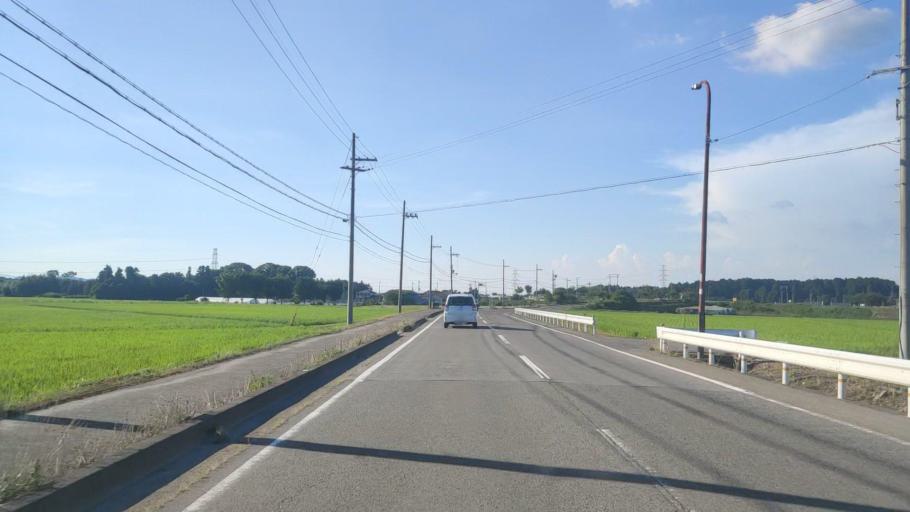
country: JP
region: Shiga Prefecture
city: Youkaichi
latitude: 35.0954
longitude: 136.2486
